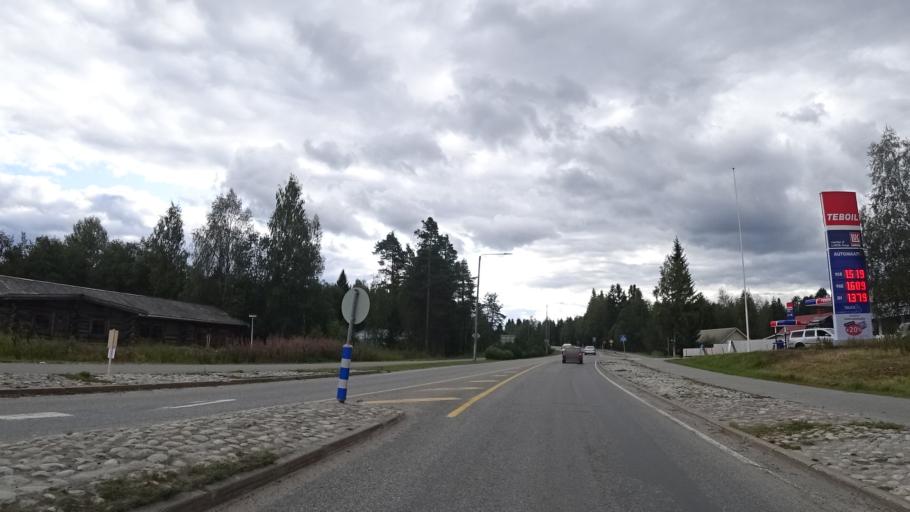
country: FI
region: North Karelia
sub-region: Joensuu
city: Ilomantsi
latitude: 62.6679
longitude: 30.9389
